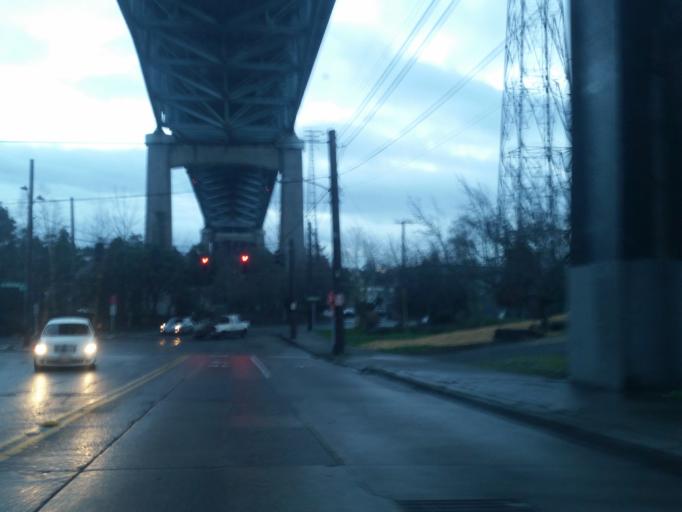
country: US
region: Washington
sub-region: King County
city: Seattle
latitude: 47.6550
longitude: -122.3226
